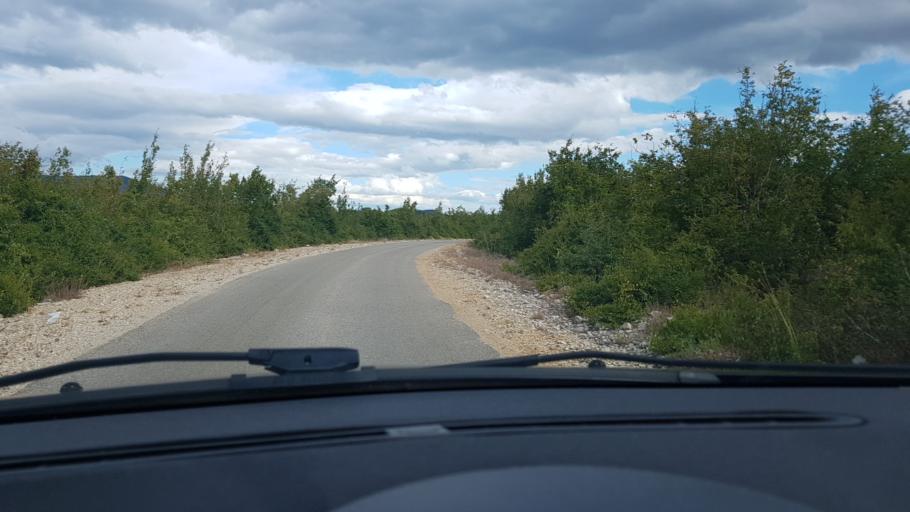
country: HR
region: Sibensko-Kniniska
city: Kistanje
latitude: 44.1132
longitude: 15.9168
